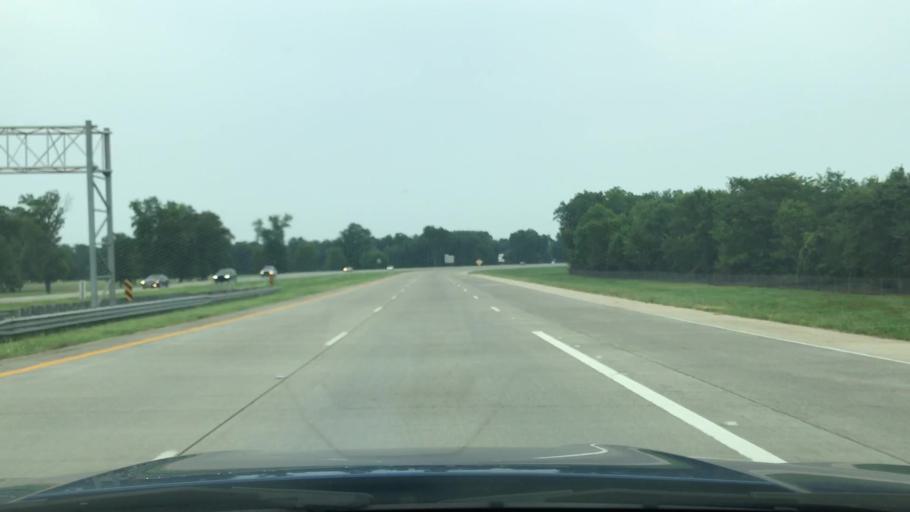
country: US
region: Louisiana
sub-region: Bossier Parish
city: Bossier City
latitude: 32.4100
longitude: -93.7206
